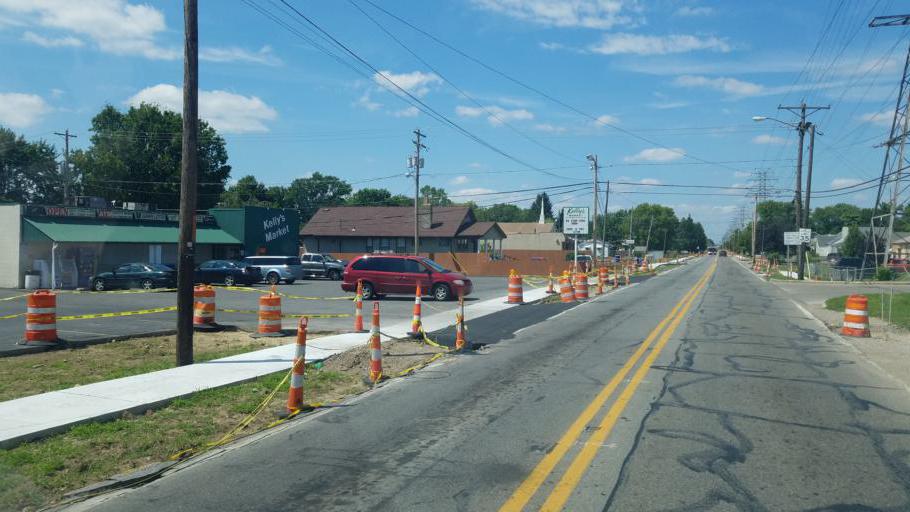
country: US
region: Ohio
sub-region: Franklin County
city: Obetz
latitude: 39.8916
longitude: -82.9870
